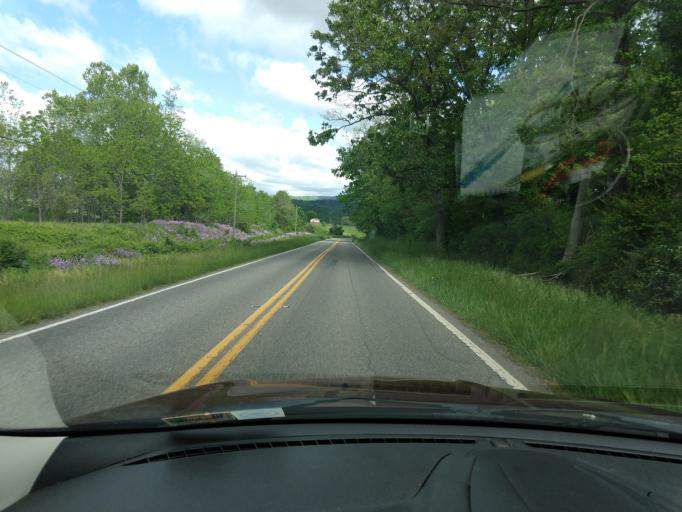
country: US
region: Virginia
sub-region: Wythe County
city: Wytheville
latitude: 36.8493
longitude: -80.9749
